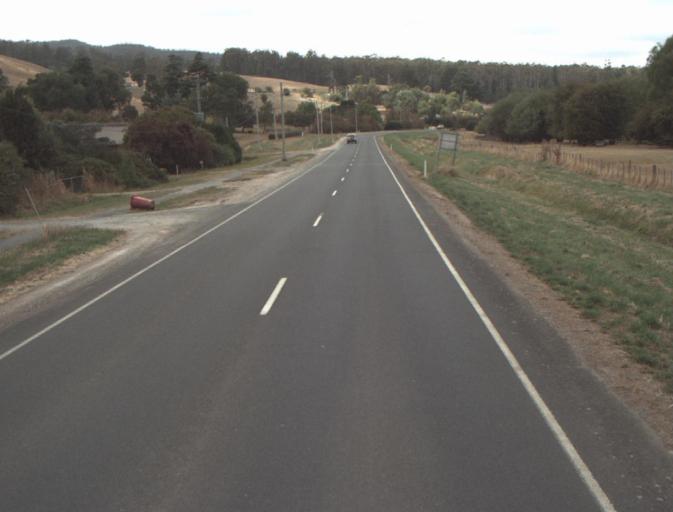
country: AU
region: Tasmania
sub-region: Launceston
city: Mayfield
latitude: -41.2565
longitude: 147.2168
